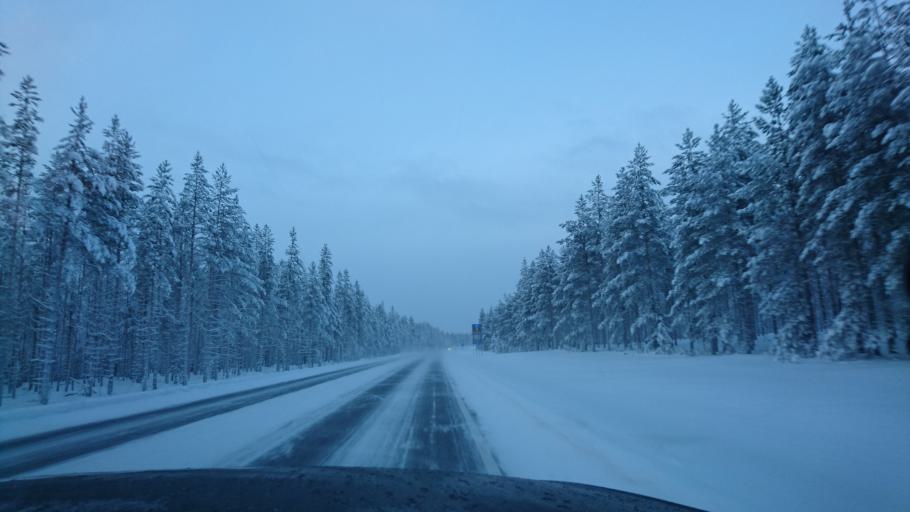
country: FI
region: Kainuu
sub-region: Kehys-Kainuu
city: Puolanka
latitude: 65.4302
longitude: 27.5534
